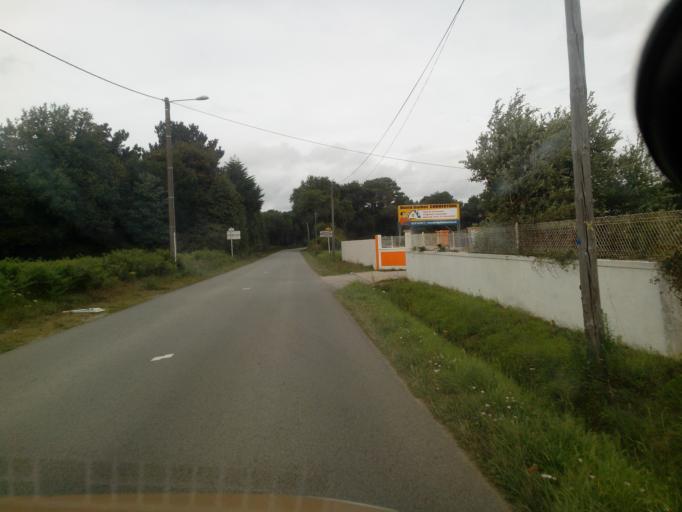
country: FR
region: Brittany
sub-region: Departement du Morbihan
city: Merlevenez
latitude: 47.7029
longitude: -3.2530
